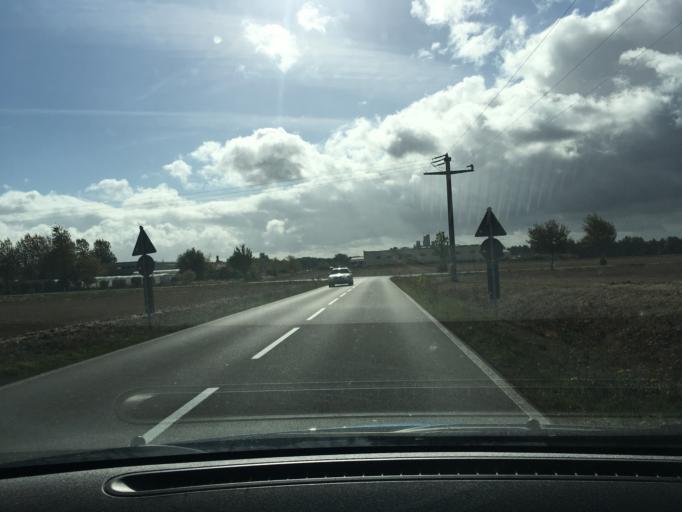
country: DE
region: Saxony-Anhalt
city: Salzwedel
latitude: 52.8553
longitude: 11.1170
